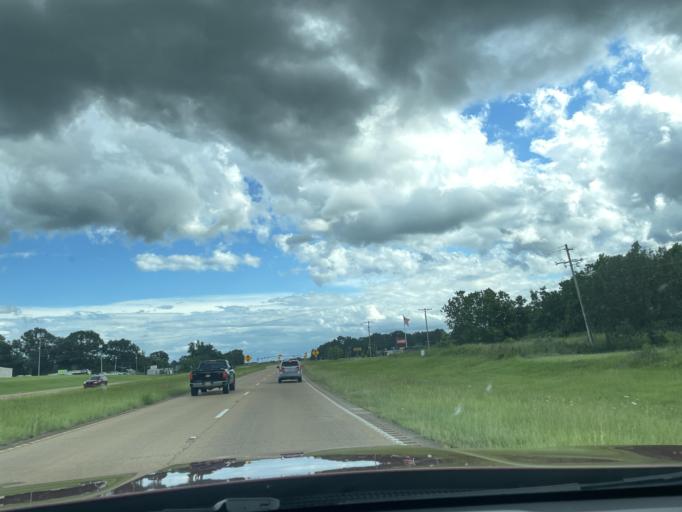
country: US
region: Mississippi
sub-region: Madison County
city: Flora
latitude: 32.5559
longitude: -90.3216
